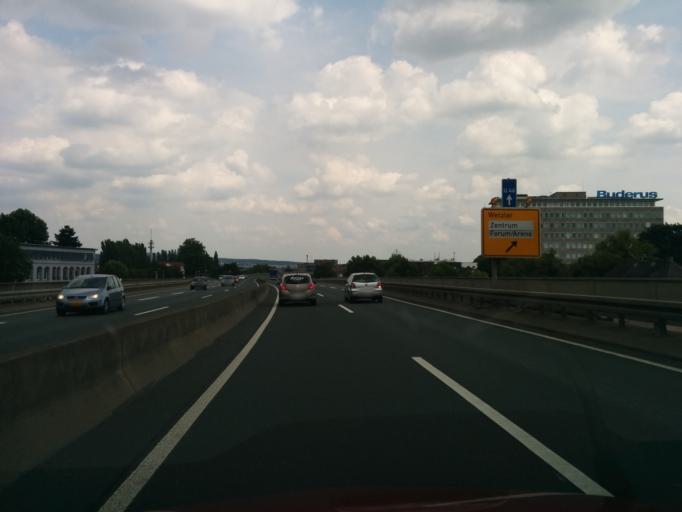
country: DE
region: Hesse
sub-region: Regierungsbezirk Giessen
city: Wetzlar
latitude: 50.5617
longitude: 8.4942
